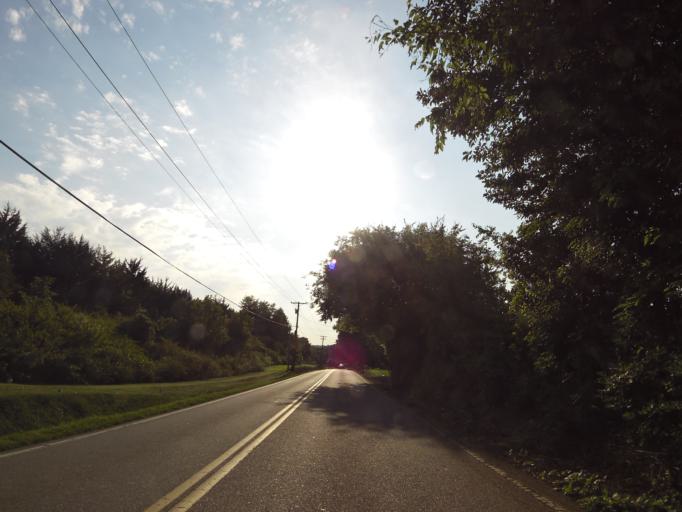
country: US
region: Tennessee
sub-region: Monroe County
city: Madisonville
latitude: 35.6001
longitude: -84.3728
